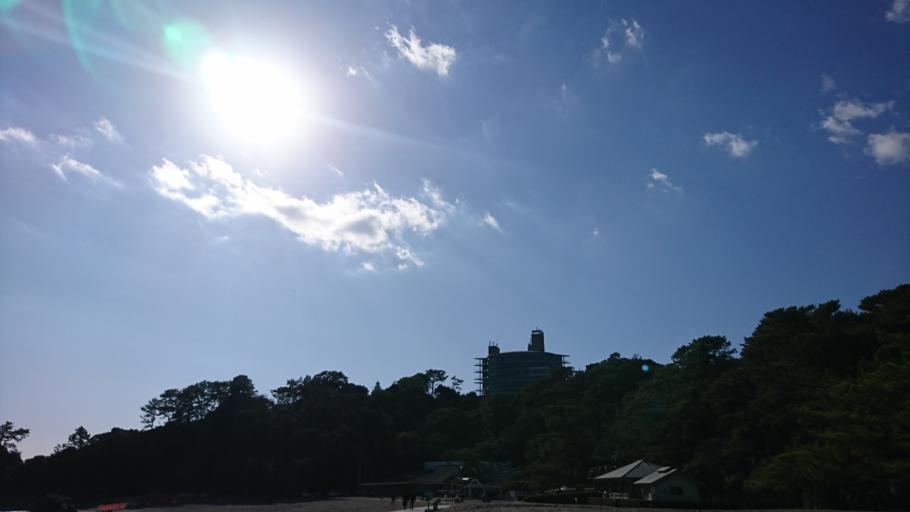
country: JP
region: Kochi
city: Kochi-shi
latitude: 33.4980
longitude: 133.5753
